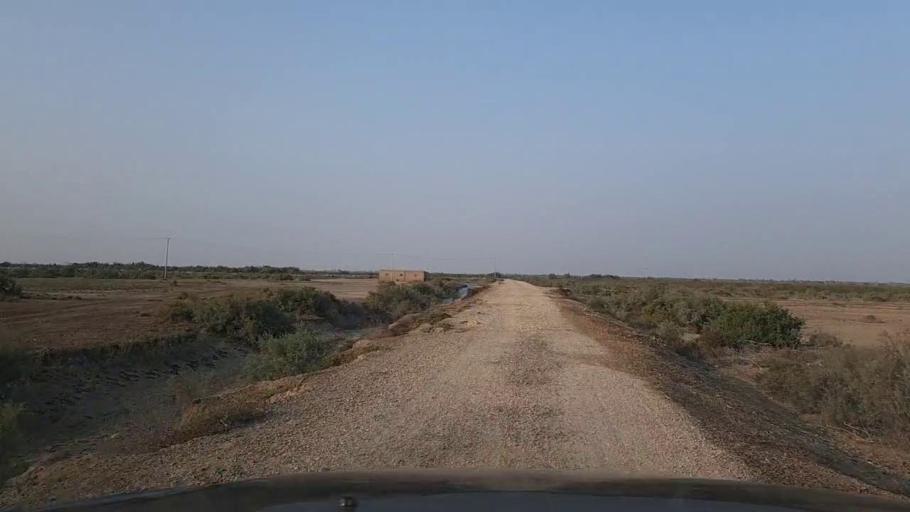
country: PK
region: Sindh
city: Mirpur Sakro
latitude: 24.4125
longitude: 67.7321
